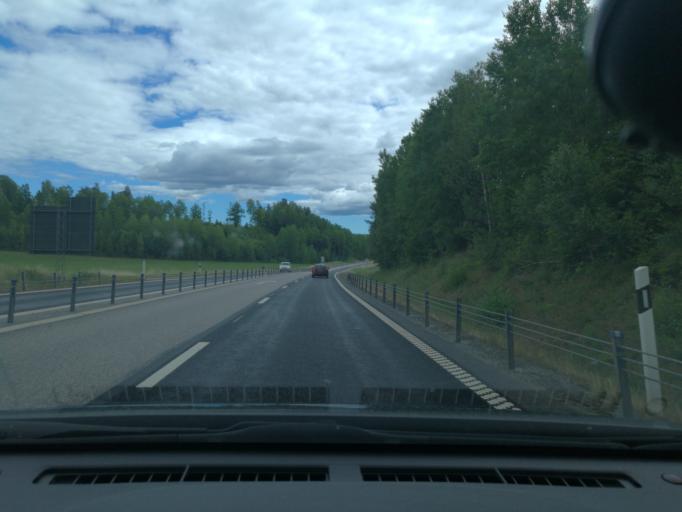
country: SE
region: OEstergoetland
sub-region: Valdemarsviks Kommun
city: Valdemarsvik
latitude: 58.2155
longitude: 16.5565
